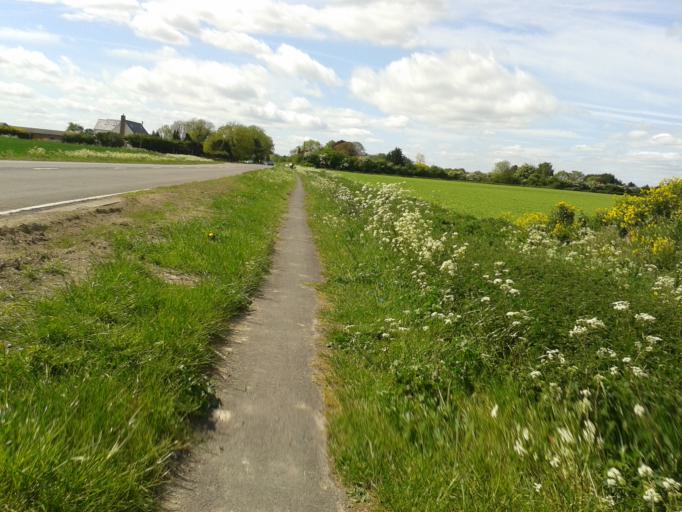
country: GB
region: England
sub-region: Cambridgeshire
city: Melbourn
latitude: 52.0976
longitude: 0.0358
